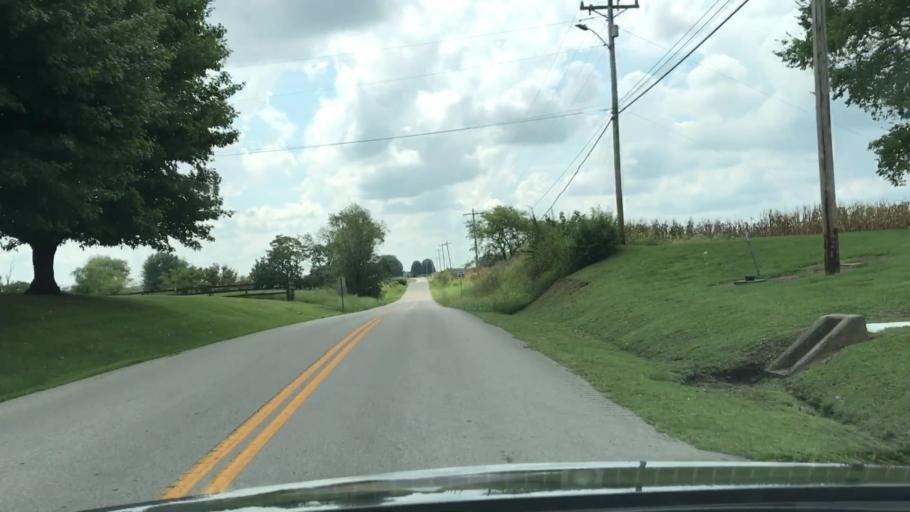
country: US
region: Kentucky
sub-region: Todd County
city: Elkton
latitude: 36.7982
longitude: -87.1487
